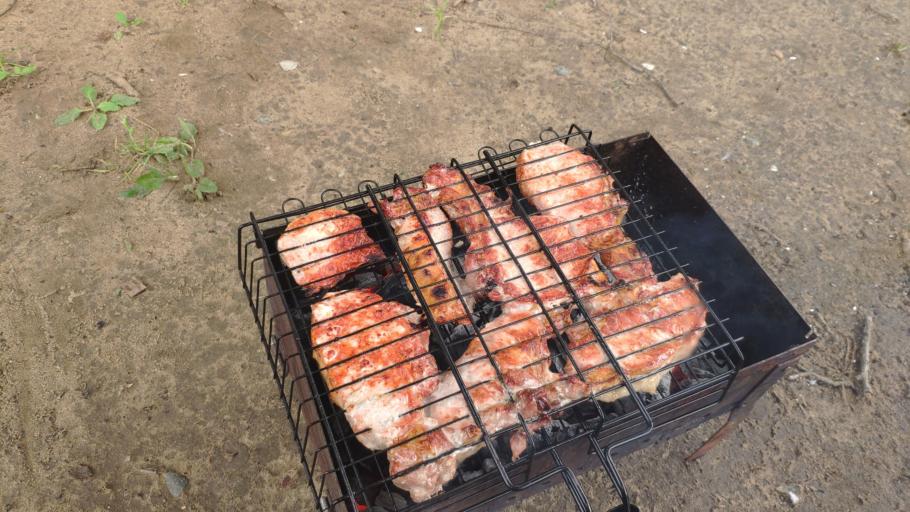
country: RU
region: Primorskiy
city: Razdol'noye
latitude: 43.5412
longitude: 131.8770
